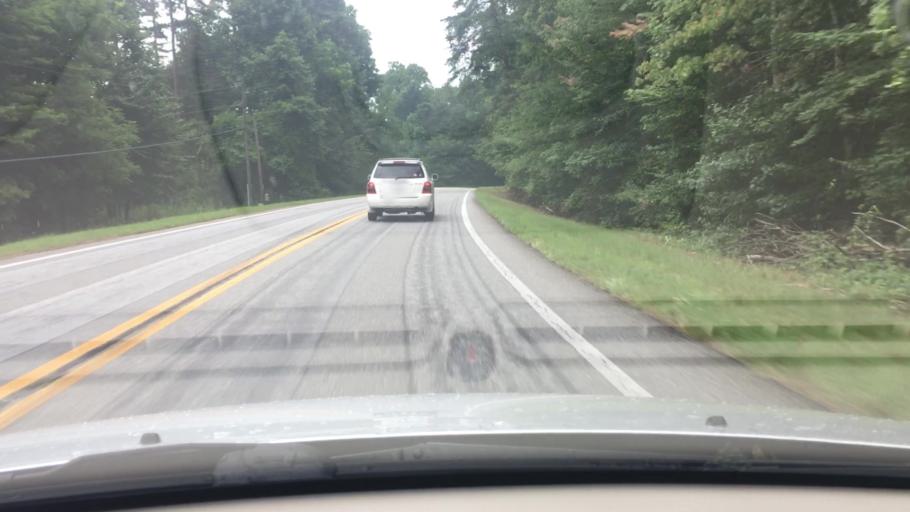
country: US
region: Georgia
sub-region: Dawson County
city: Dawsonville
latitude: 34.4321
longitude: -84.0572
